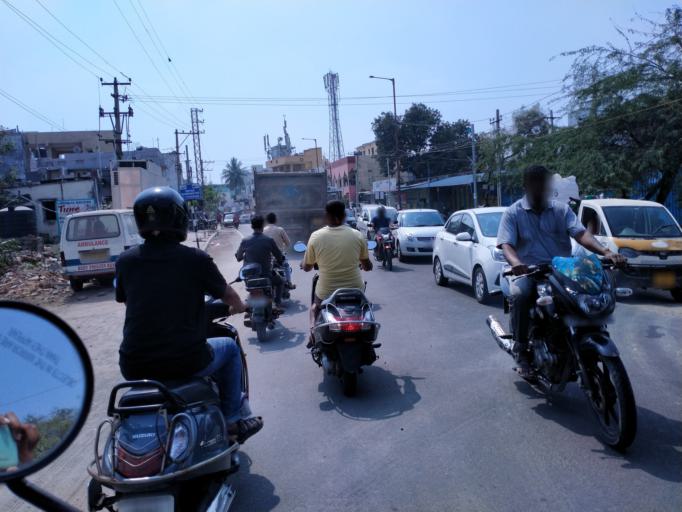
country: IN
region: Telangana
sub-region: Rangareddi
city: Secunderabad
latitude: 17.4767
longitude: 78.5376
